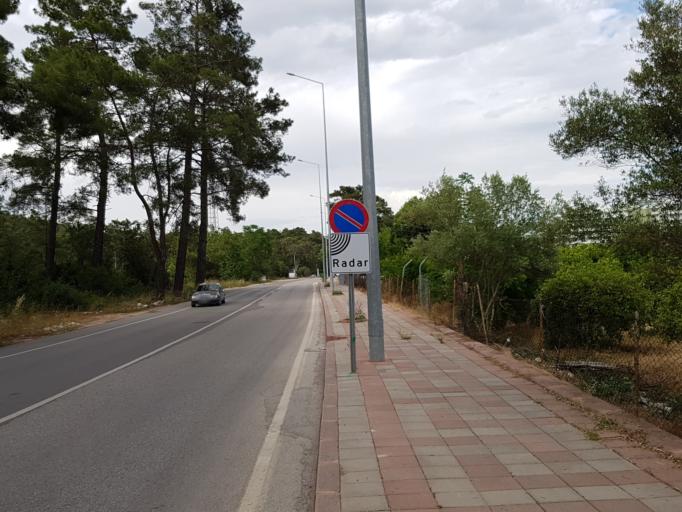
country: TR
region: Antalya
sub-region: Kemer
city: Goeynuek
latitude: 36.6444
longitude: 30.5481
